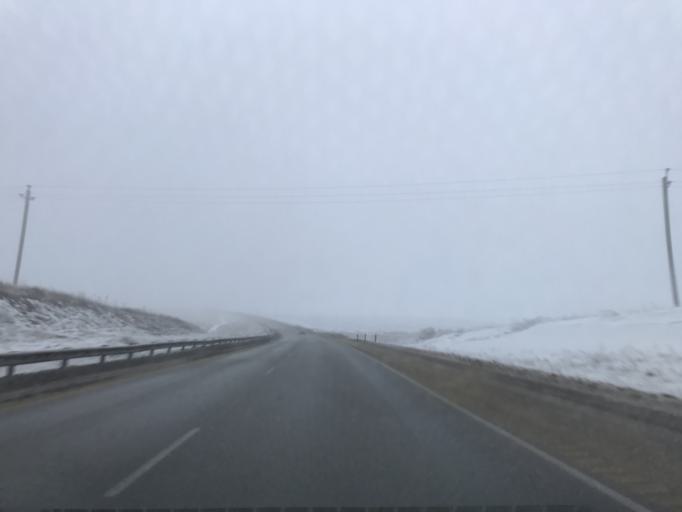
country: RU
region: Rostov
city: Temernik
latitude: 47.3652
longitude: 39.7649
